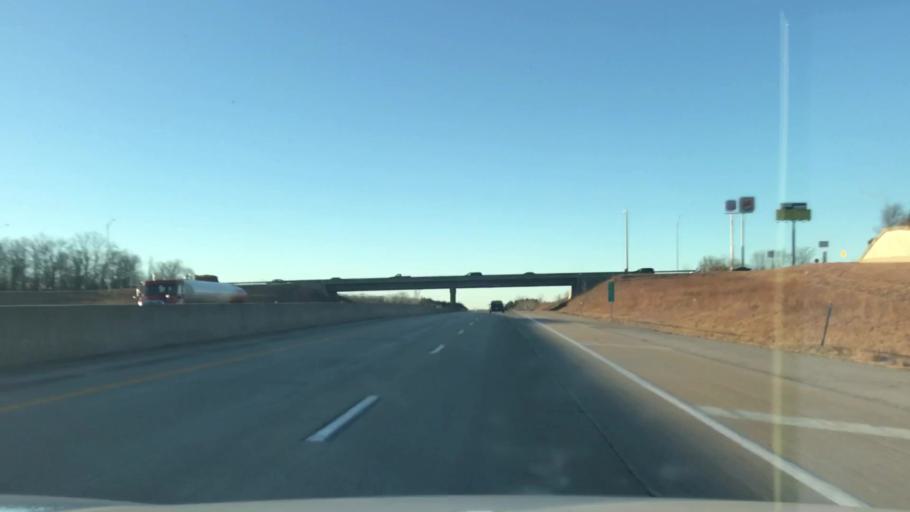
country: US
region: Missouri
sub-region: Franklin County
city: Gray Summit
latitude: 38.4760
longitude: -90.8496
